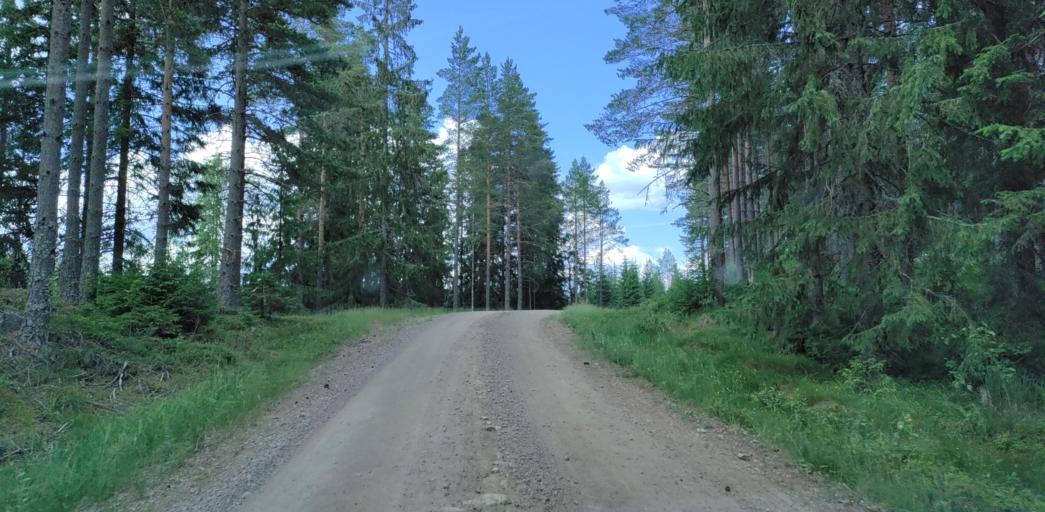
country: SE
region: Vaermland
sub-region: Hagfors Kommun
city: Ekshaerad
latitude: 60.0840
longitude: 13.3449
